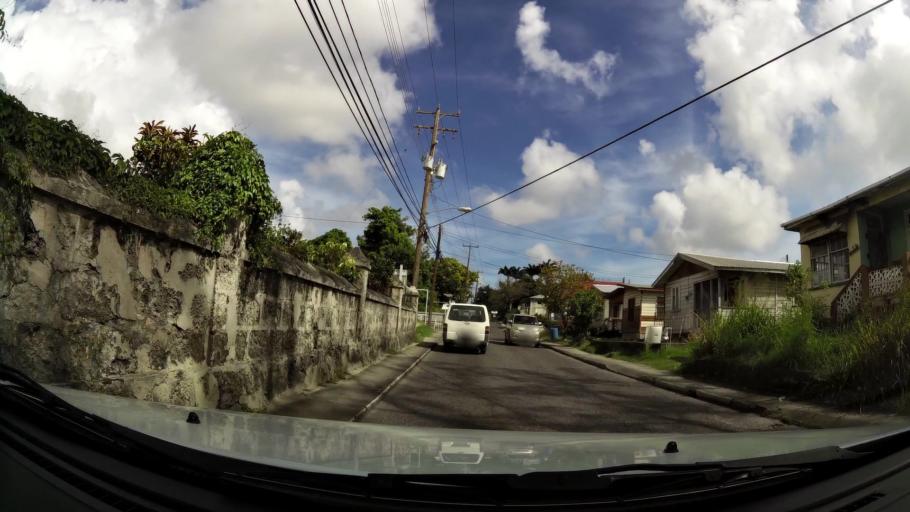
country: BB
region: Saint Michael
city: Bridgetown
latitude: 13.0938
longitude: -59.5972
